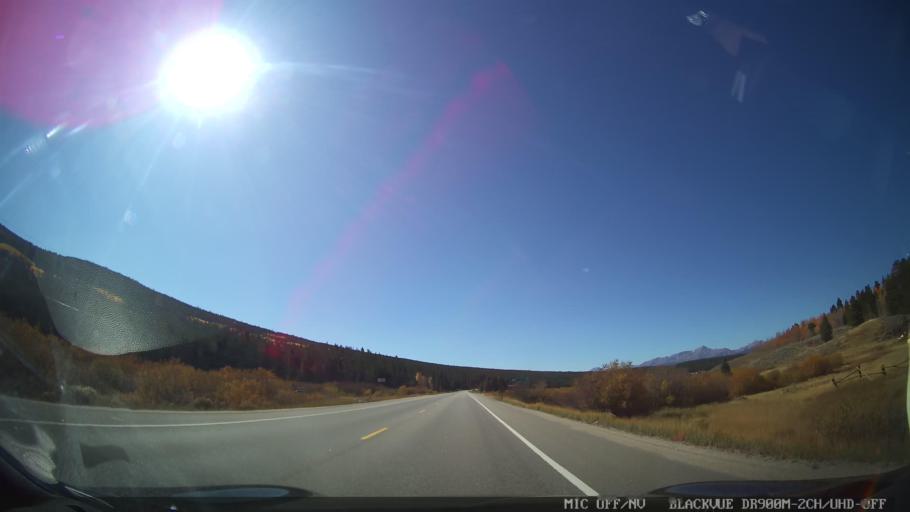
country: US
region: Colorado
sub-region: Lake County
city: Leadville North
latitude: 39.2869
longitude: -106.2803
